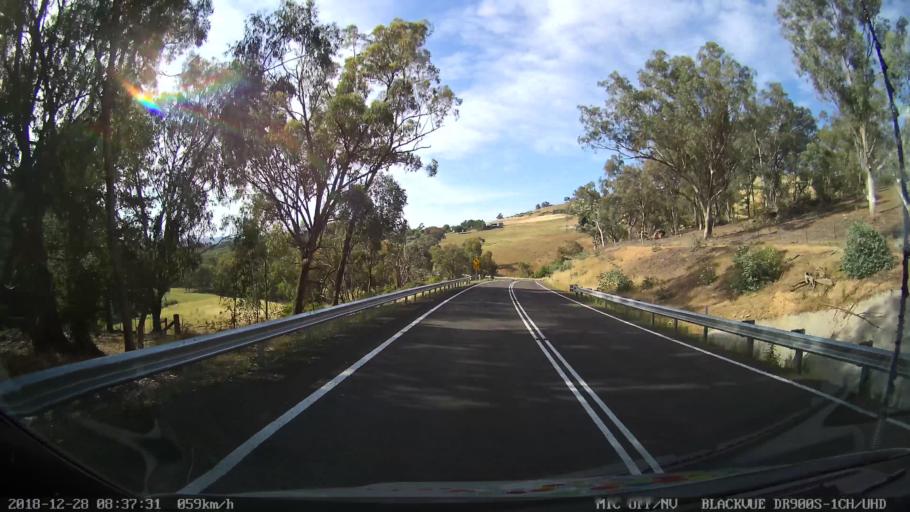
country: AU
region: New South Wales
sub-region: Blayney
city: Blayney
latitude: -33.9960
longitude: 149.3132
